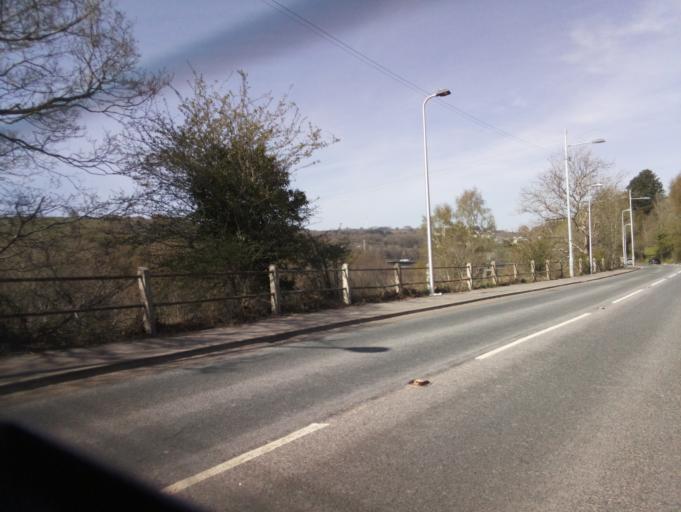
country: GB
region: Wales
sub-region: Merthyr Tydfil County Borough
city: Treharris
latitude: 51.6500
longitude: -3.3132
